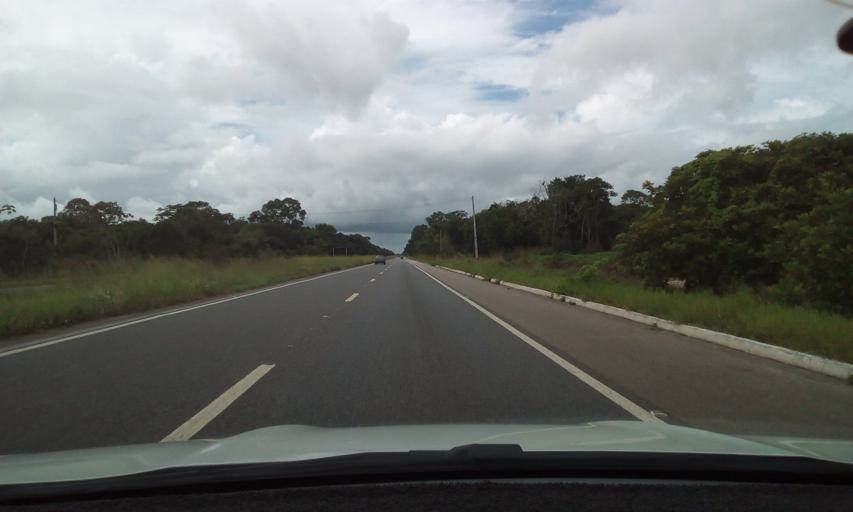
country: BR
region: Paraiba
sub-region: Cruz Do Espirito Santo
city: Cruz do Espirito Santo
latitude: -7.2025
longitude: -35.1073
